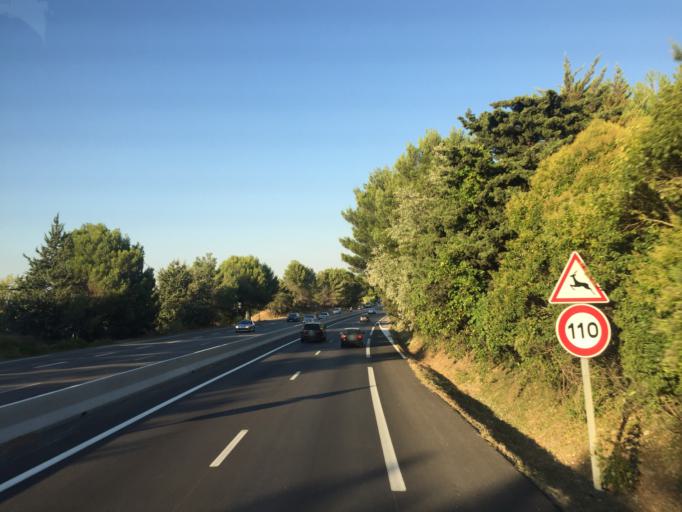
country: FR
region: Provence-Alpes-Cote d'Azur
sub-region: Departement des Bouches-du-Rhone
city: Aix-en-Provence
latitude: 43.5607
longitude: 5.4540
